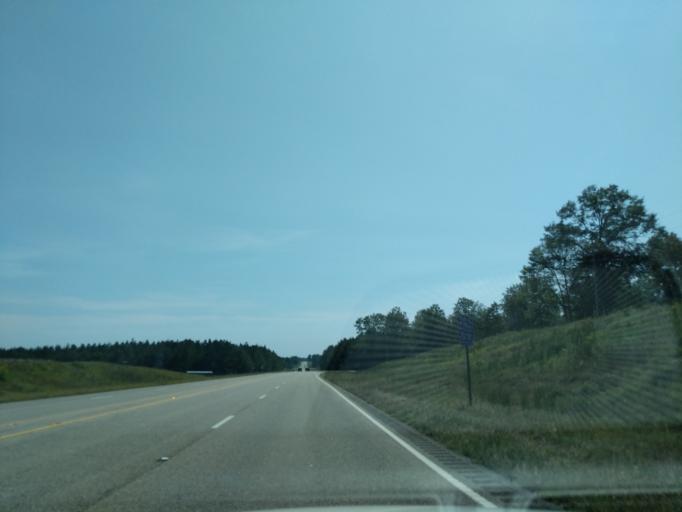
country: US
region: Alabama
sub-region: Covington County
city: Andalusia
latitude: 31.3853
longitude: -86.5698
